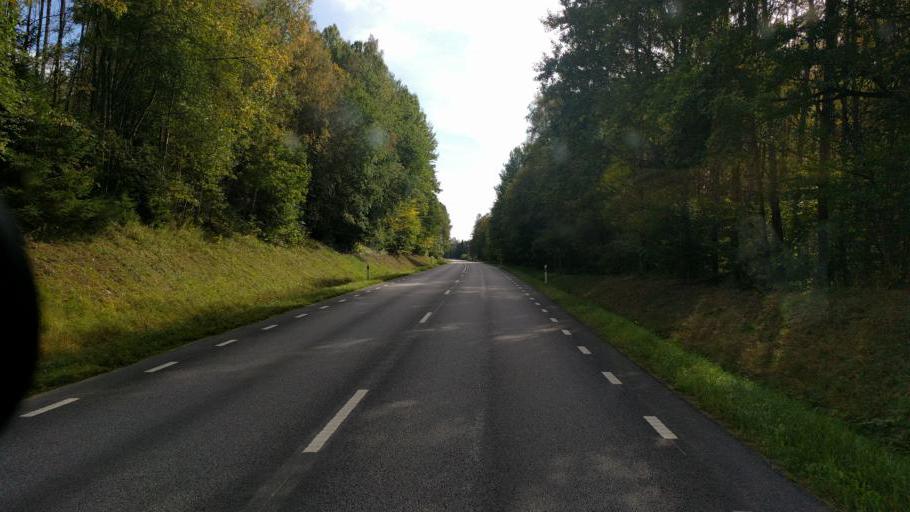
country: SE
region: OEstergoetland
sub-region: Kinda Kommun
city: Kisa
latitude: 57.9381
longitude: 15.6678
